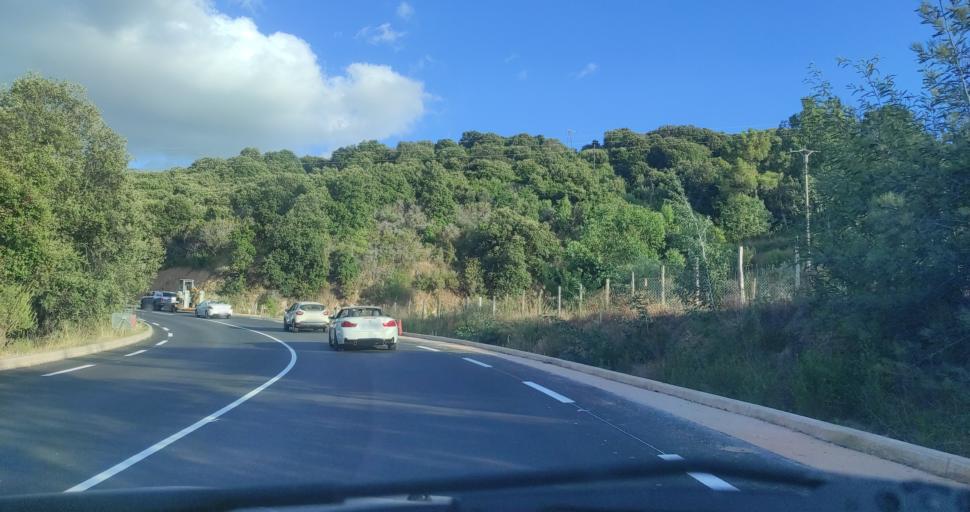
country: FR
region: Corsica
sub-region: Departement de la Corse-du-Sud
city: Appietto
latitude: 42.0362
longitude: 8.7526
